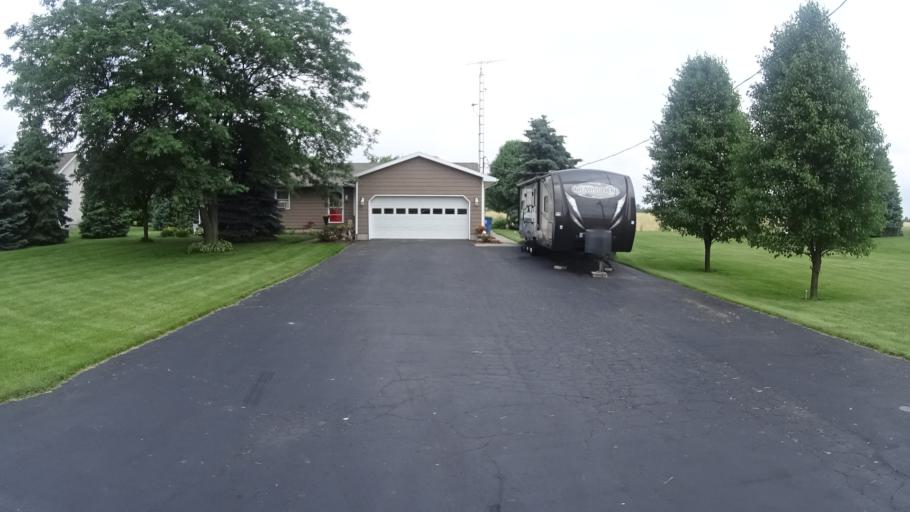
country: US
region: Ohio
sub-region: Huron County
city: Bellevue
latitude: 41.2949
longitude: -82.8168
